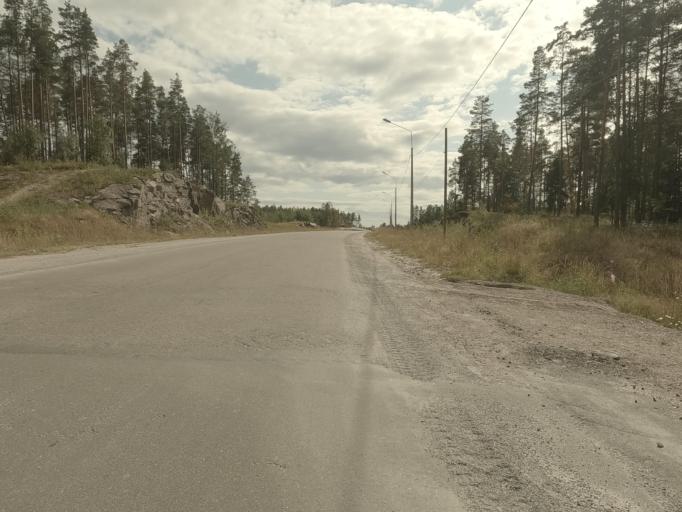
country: RU
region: Leningrad
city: Kamennogorsk
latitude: 60.9611
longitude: 29.1409
